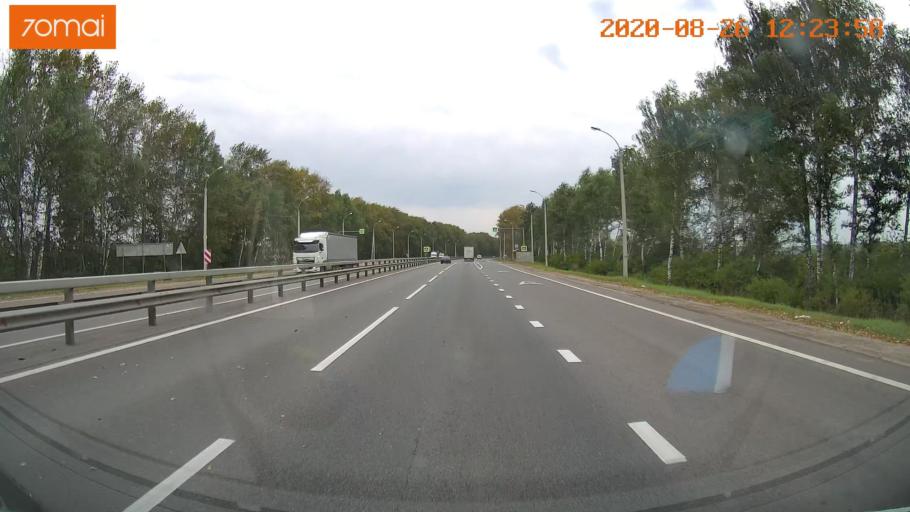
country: RU
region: Rjazan
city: Murmino
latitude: 54.5090
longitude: 39.9009
